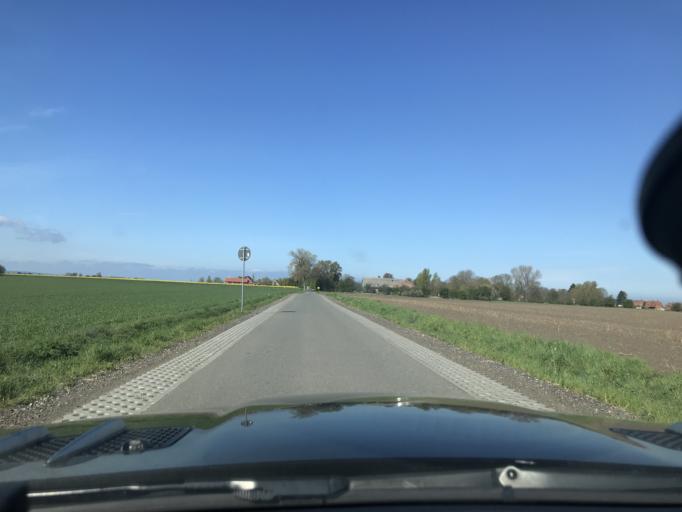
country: DE
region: Schleswig-Holstein
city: Grossenbrode
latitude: 54.4260
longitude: 11.1169
